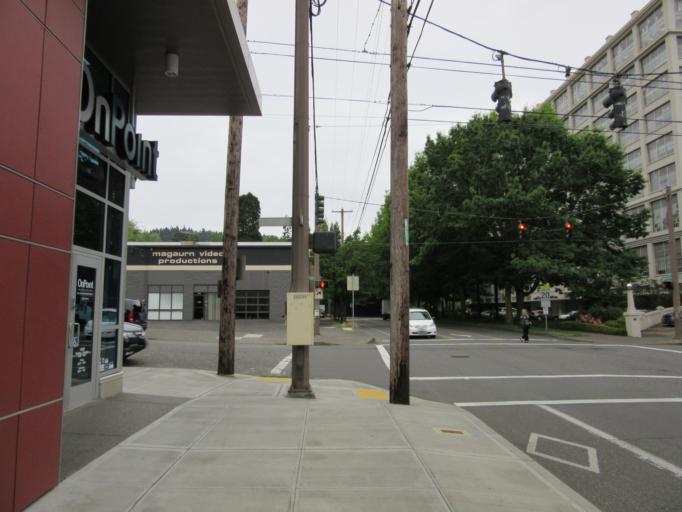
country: US
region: Oregon
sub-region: Multnomah County
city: Portland
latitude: 45.5367
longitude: -122.7067
